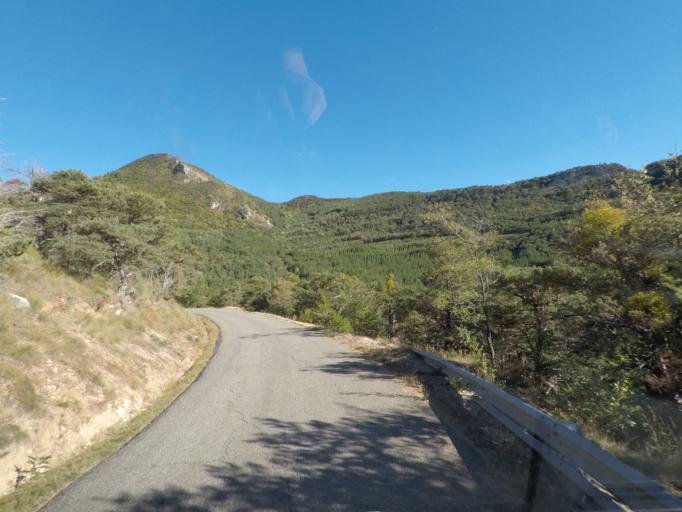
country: FR
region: Provence-Alpes-Cote d'Azur
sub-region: Departement des Hautes-Alpes
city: Serres
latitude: 44.4372
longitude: 5.5673
